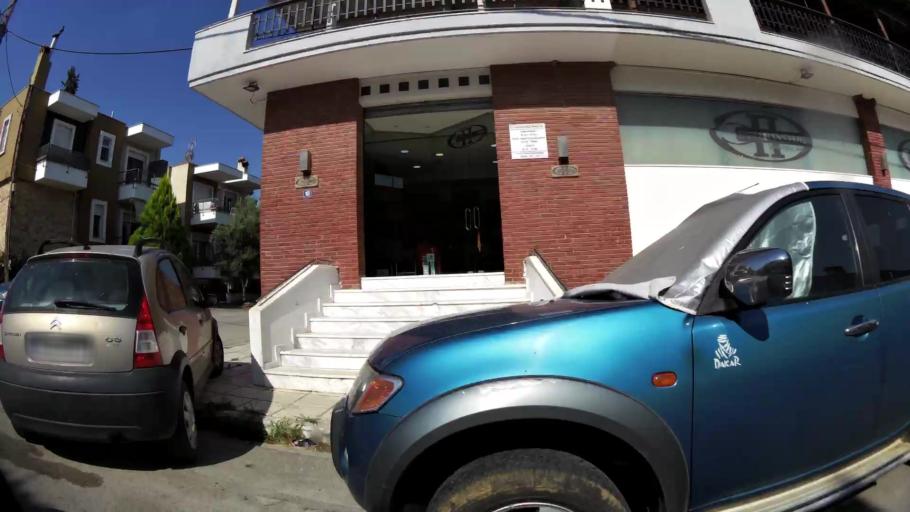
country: GR
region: Central Macedonia
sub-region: Nomos Thessalonikis
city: Neo Rysi
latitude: 40.4961
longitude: 22.9906
